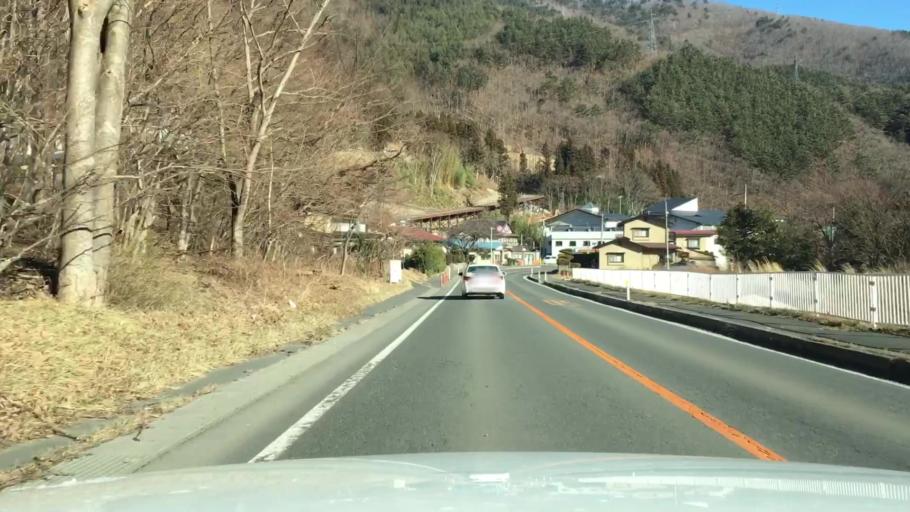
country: JP
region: Iwate
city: Miyako
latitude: 39.5971
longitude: 141.6771
